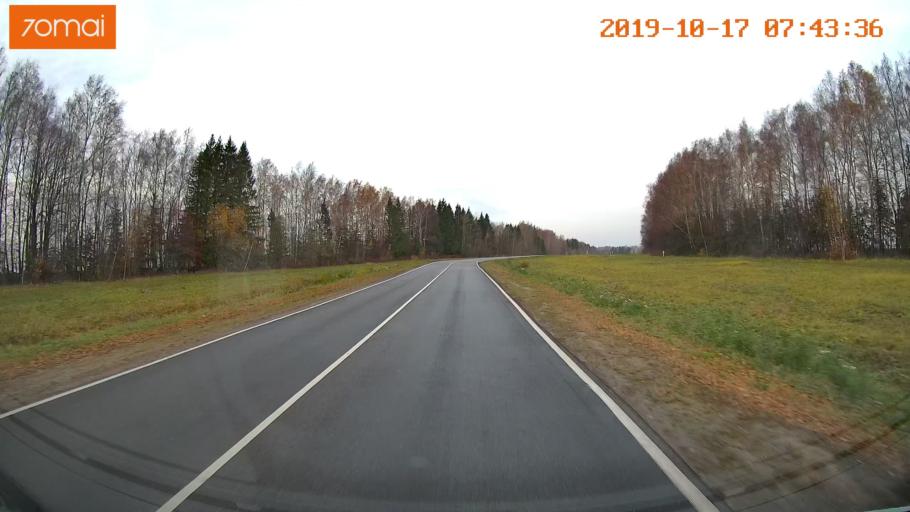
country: RU
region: Vladimir
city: Yur'yev-Pol'skiy
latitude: 56.4832
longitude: 39.7606
